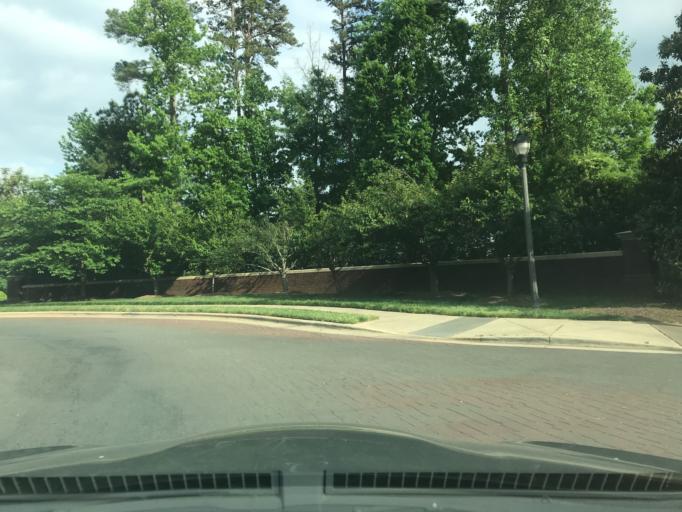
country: US
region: North Carolina
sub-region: Wake County
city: Wake Forest
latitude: 35.9242
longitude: -78.5763
